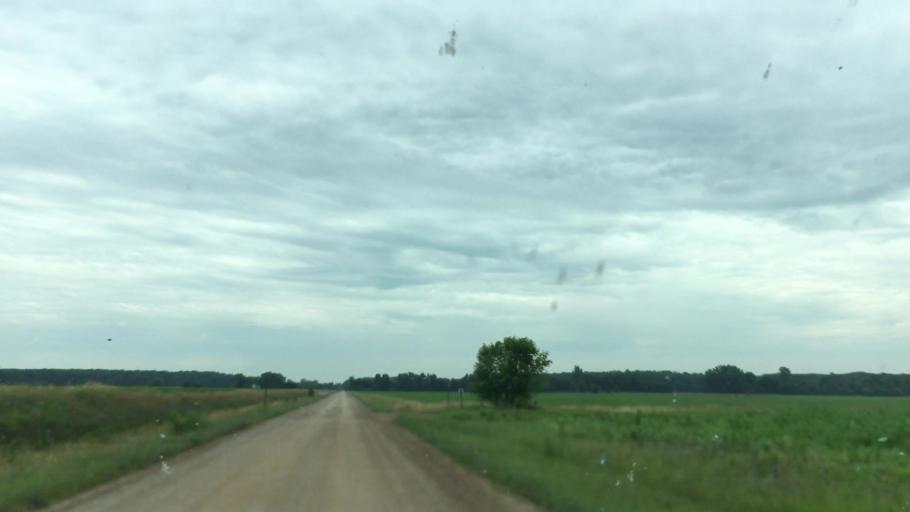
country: US
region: Michigan
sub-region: Clinton County
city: Saint Johns
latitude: 43.0740
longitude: -84.4840
